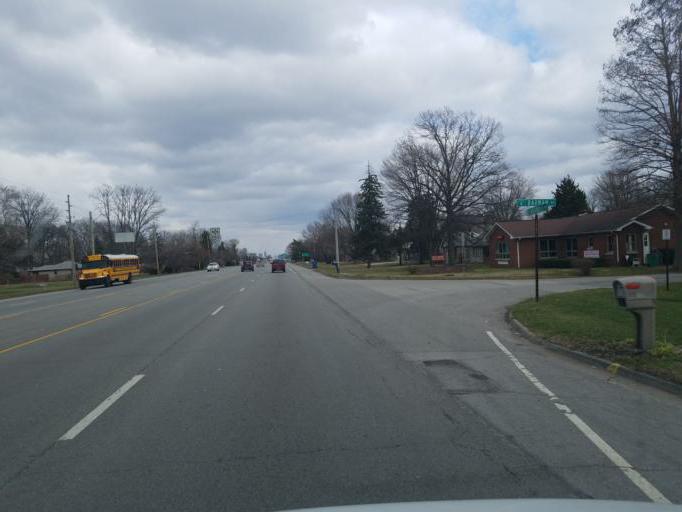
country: US
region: Indiana
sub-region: Marion County
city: Speedway
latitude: 39.7644
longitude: -86.2798
